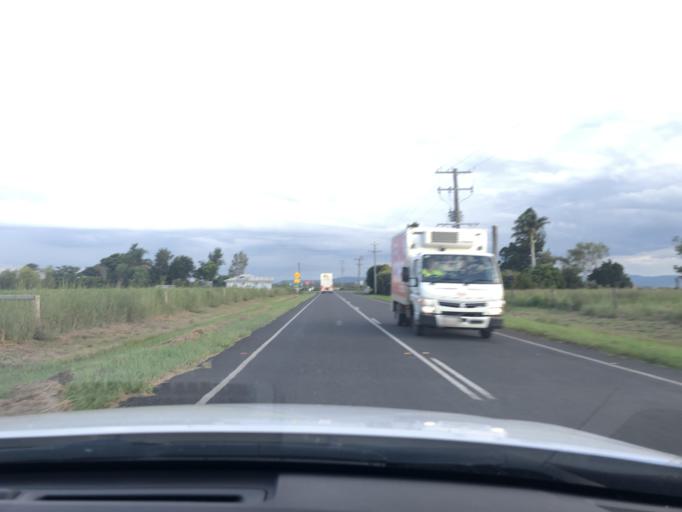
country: AU
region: Queensland
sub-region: Lockyer Valley
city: Gatton
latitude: -27.5823
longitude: 152.3631
